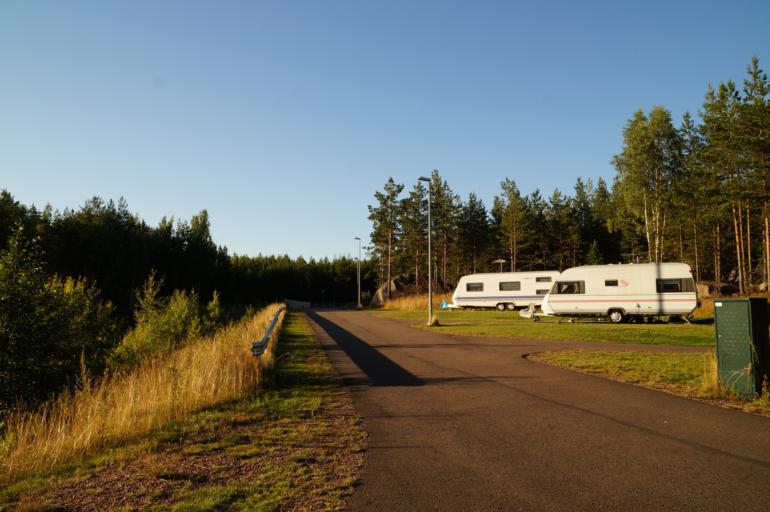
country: FI
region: Kymenlaakso
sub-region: Kotka-Hamina
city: Kotka
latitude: 60.4373
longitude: 26.8587
